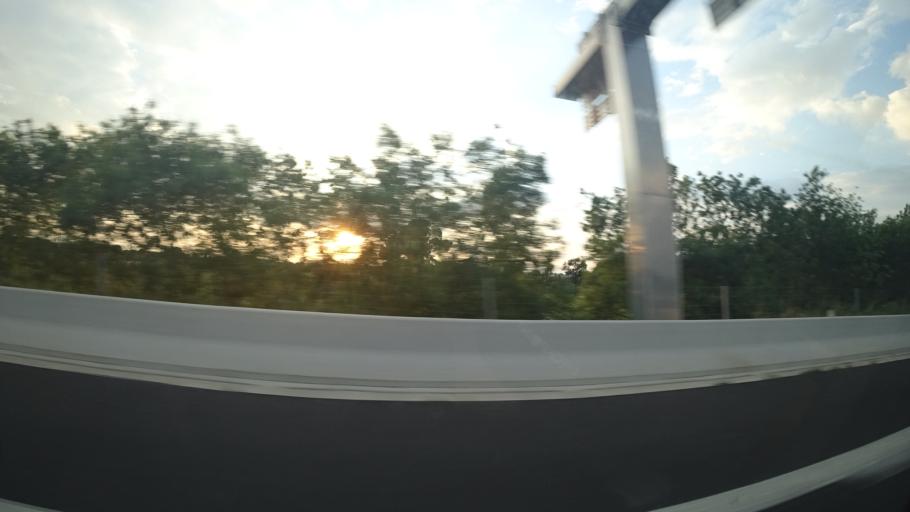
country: FR
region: Languedoc-Roussillon
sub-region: Departement de l'Herault
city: Pezenas
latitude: 43.4492
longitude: 3.4275
